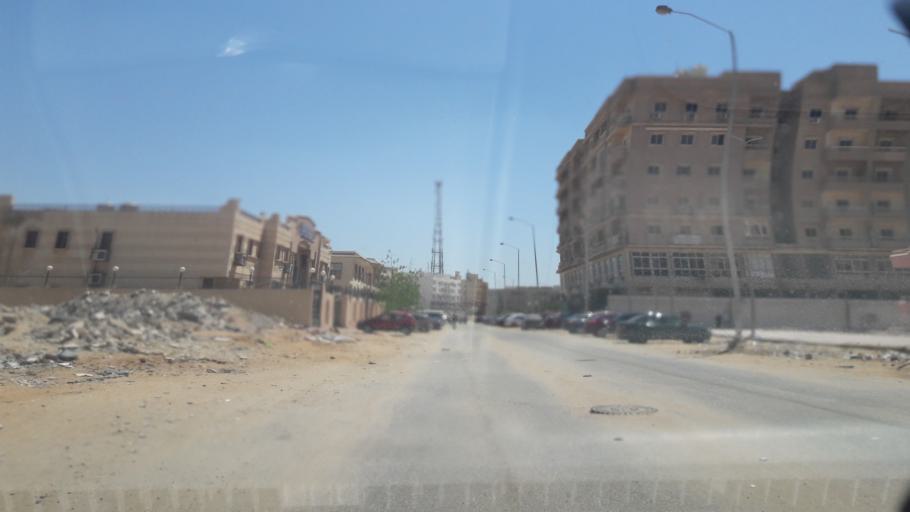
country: EG
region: Al Jizah
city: Madinat Sittah Uktubar
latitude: 29.9664
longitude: 30.9321
